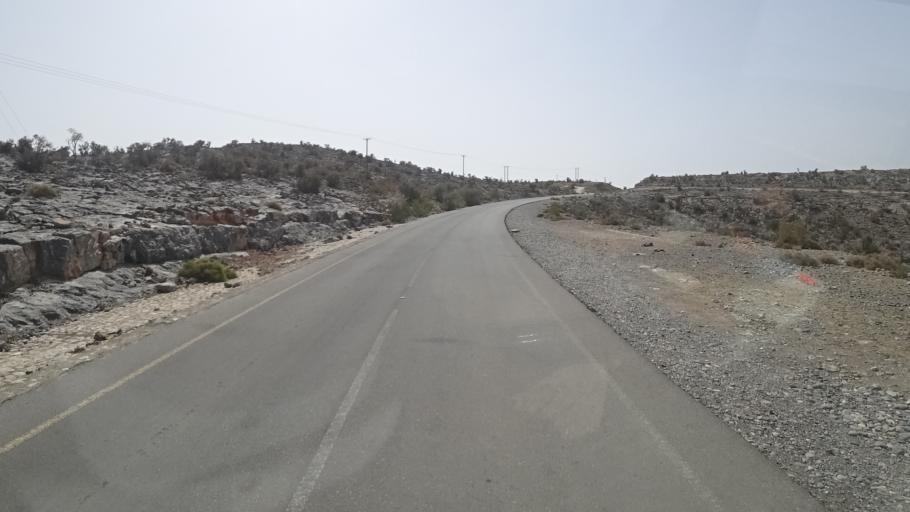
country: OM
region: Al Batinah
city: Bayt al `Awabi
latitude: 23.1493
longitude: 57.4232
